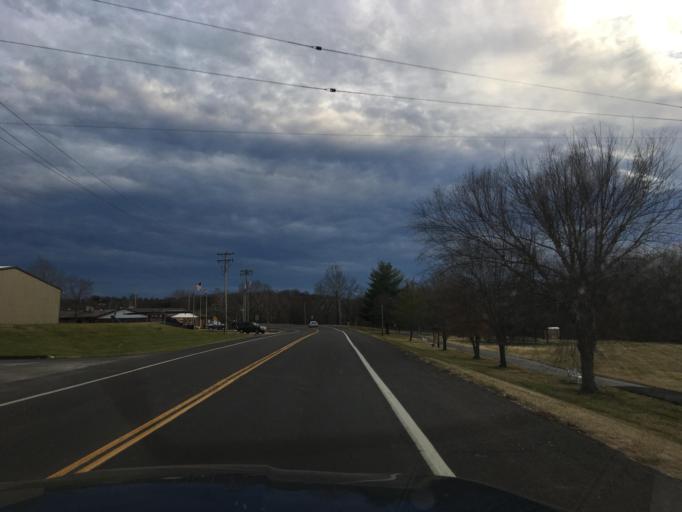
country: US
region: Missouri
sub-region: Jefferson County
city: De Soto
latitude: 38.1188
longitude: -90.5604
